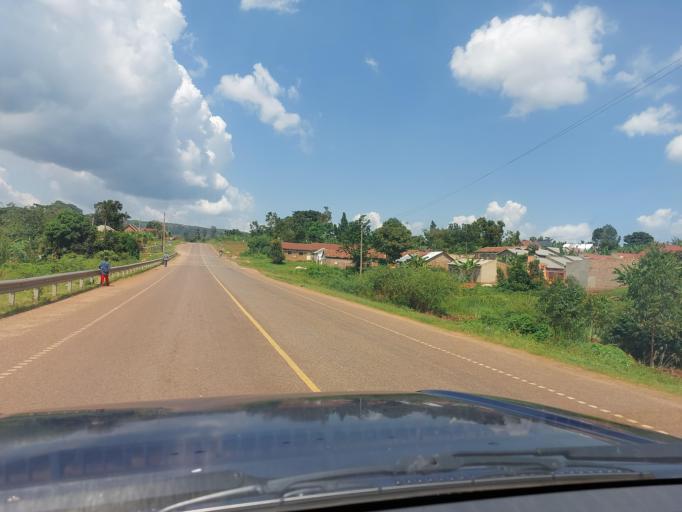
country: UG
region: Central Region
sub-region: Buikwe District
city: Buikwe
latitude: 0.3137
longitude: 33.1055
